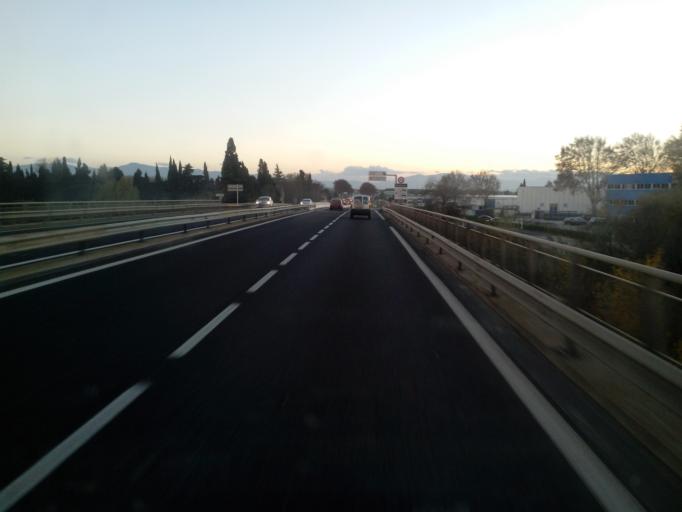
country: FR
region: Languedoc-Roussillon
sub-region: Departement des Pyrenees-Orientales
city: Rivesaltes
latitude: 42.7728
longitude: 2.9013
